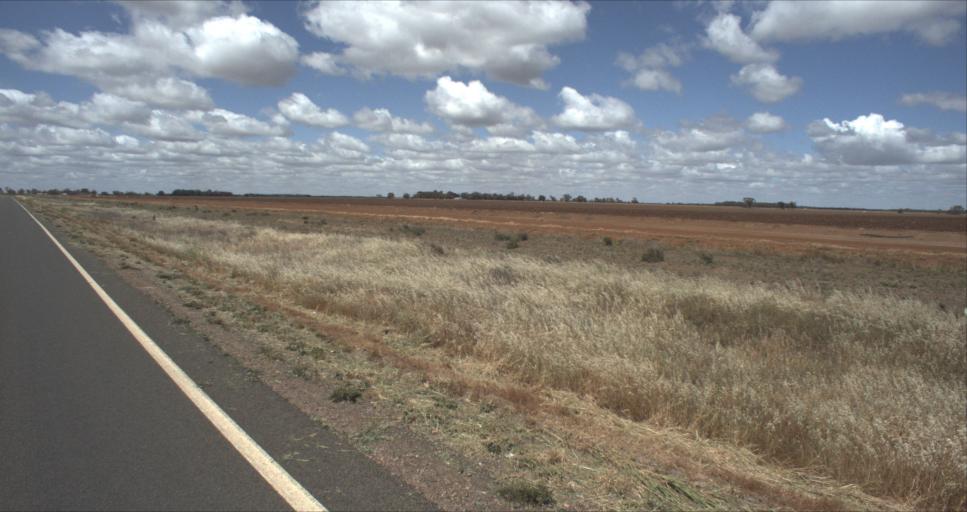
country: AU
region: New South Wales
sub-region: Murrumbidgee Shire
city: Darlington Point
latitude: -34.4708
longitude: 146.1400
